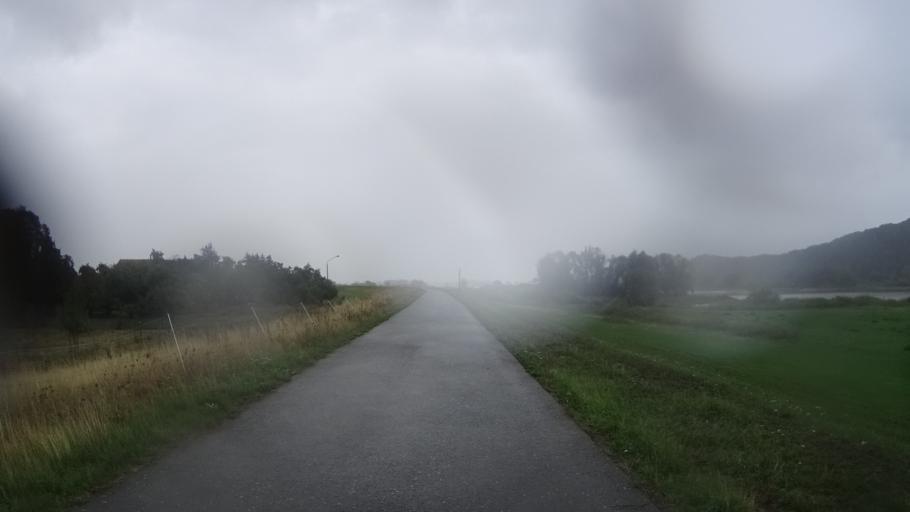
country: DE
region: Lower Saxony
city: Hitzacker
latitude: 53.1672
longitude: 11.0350
